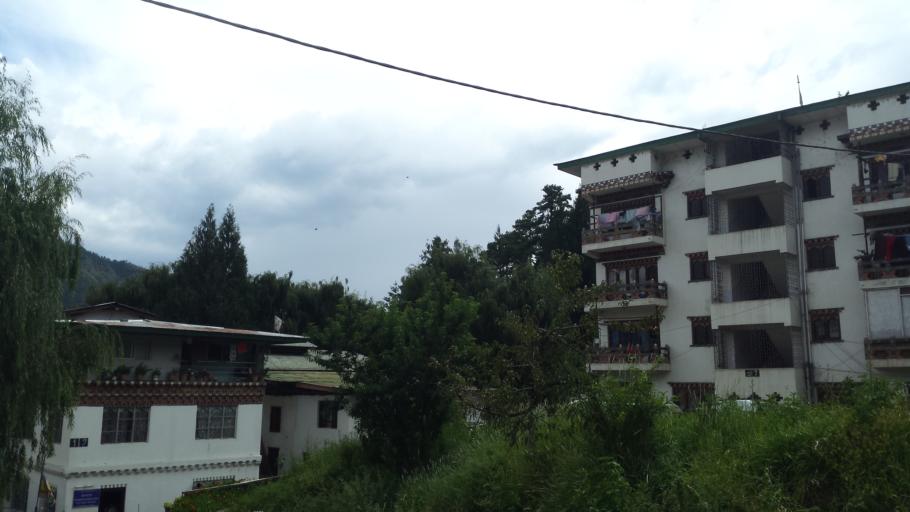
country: BT
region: Thimphu
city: Thimphu
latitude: 27.4746
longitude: 89.6277
